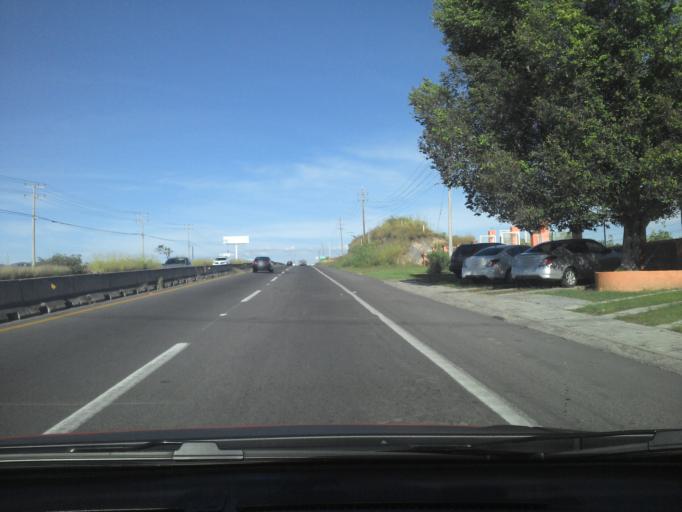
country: MX
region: Jalisco
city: Tala
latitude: 20.6719
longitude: -103.7112
